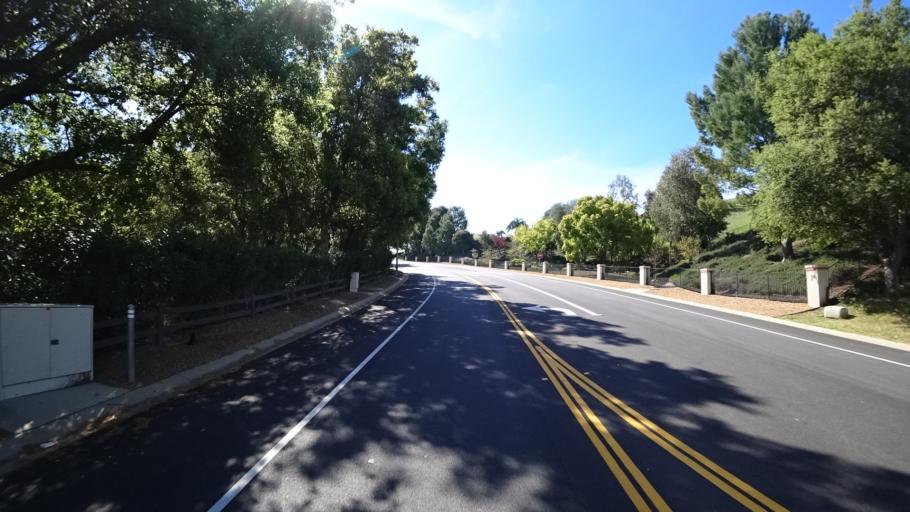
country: US
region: California
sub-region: Ventura County
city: Thousand Oaks
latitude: 34.1895
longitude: -118.8090
